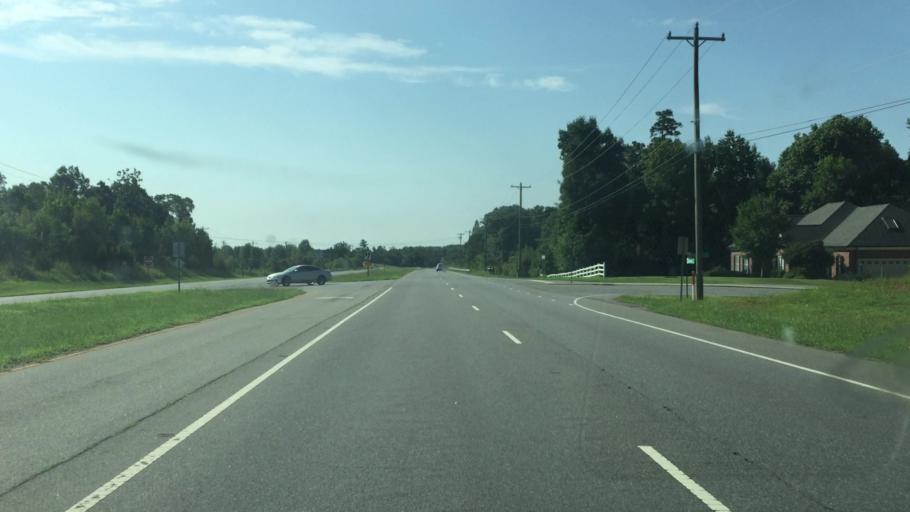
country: US
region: North Carolina
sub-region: Cabarrus County
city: Kannapolis
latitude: 35.4658
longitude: -80.6684
